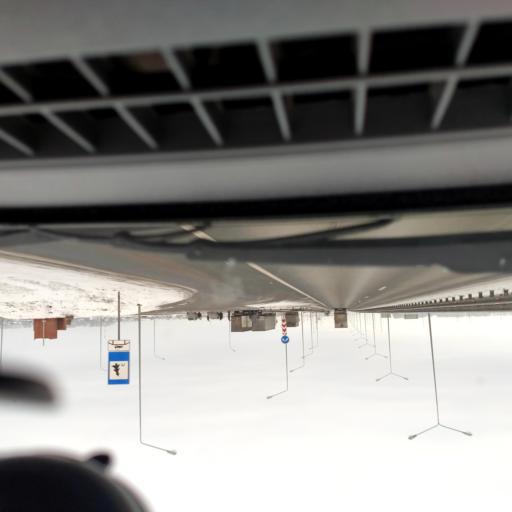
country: RU
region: Bashkortostan
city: Kushnarenkovo
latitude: 55.0725
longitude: 55.2884
